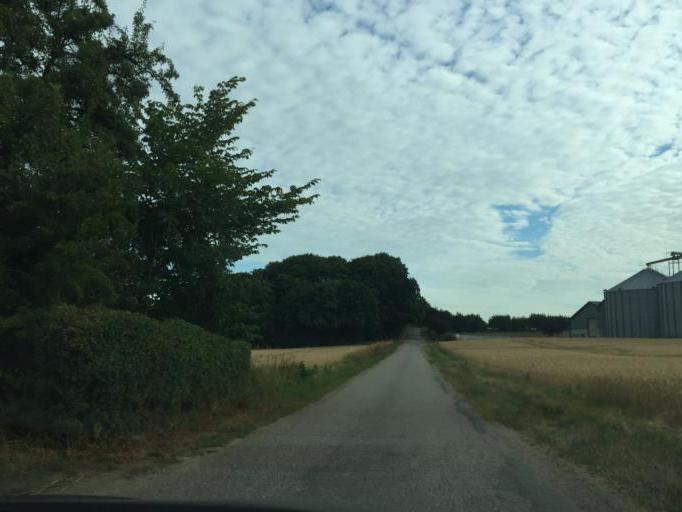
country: DK
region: South Denmark
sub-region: Assens Kommune
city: Assens
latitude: 55.2687
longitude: 9.9704
